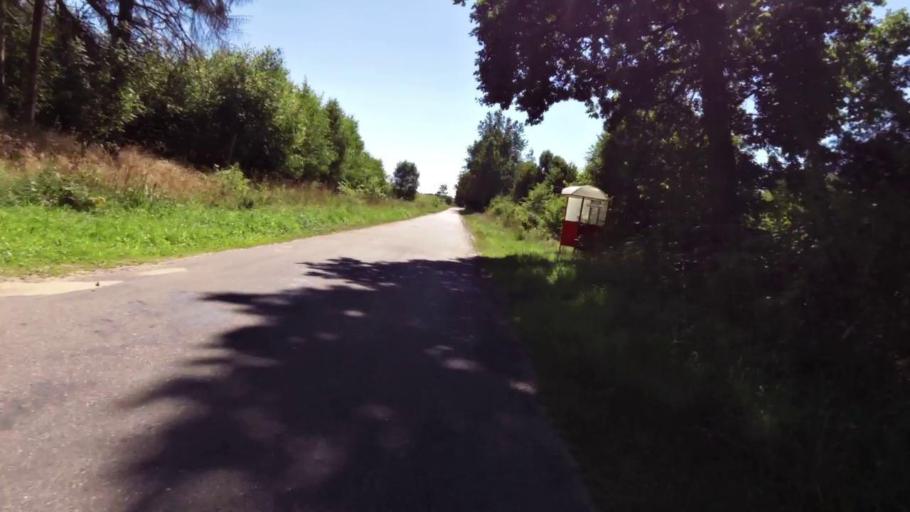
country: PL
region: West Pomeranian Voivodeship
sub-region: Powiat szczecinecki
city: Bialy Bor
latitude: 53.9366
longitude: 16.8535
